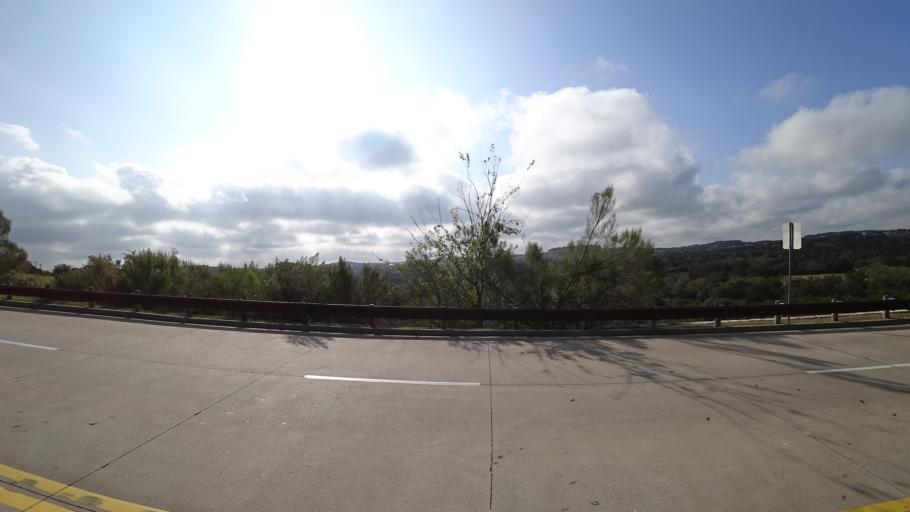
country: US
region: Texas
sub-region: Travis County
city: Bee Cave
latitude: 30.3046
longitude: -97.9369
